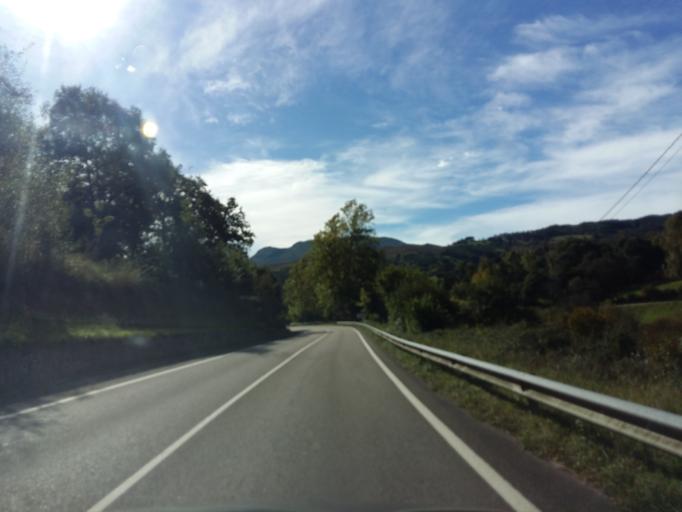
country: ES
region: Cantabria
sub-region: Provincia de Cantabria
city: San Vicente de la Barquera
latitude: 43.3124
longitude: -4.4714
